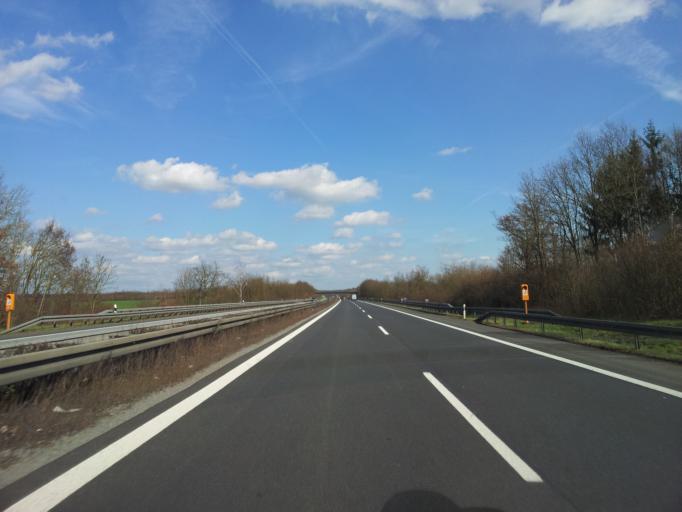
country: DE
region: Bavaria
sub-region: Regierungsbezirk Unterfranken
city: Wonfurt
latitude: 50.0040
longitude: 10.4554
